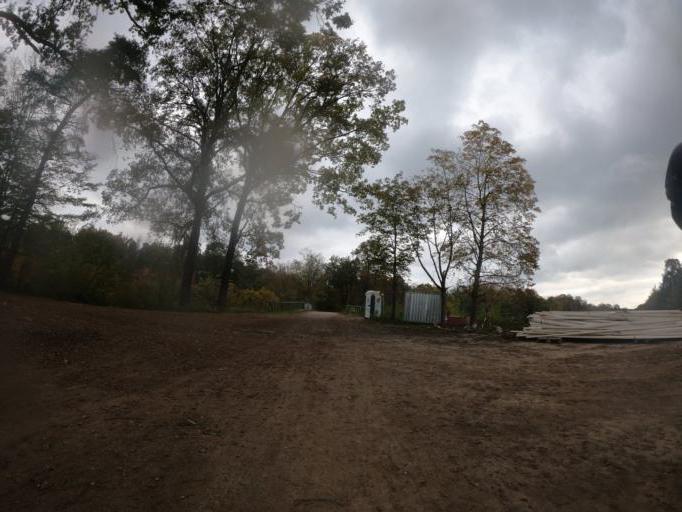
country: DE
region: Hesse
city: Niederrad
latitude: 50.0659
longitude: 8.5957
